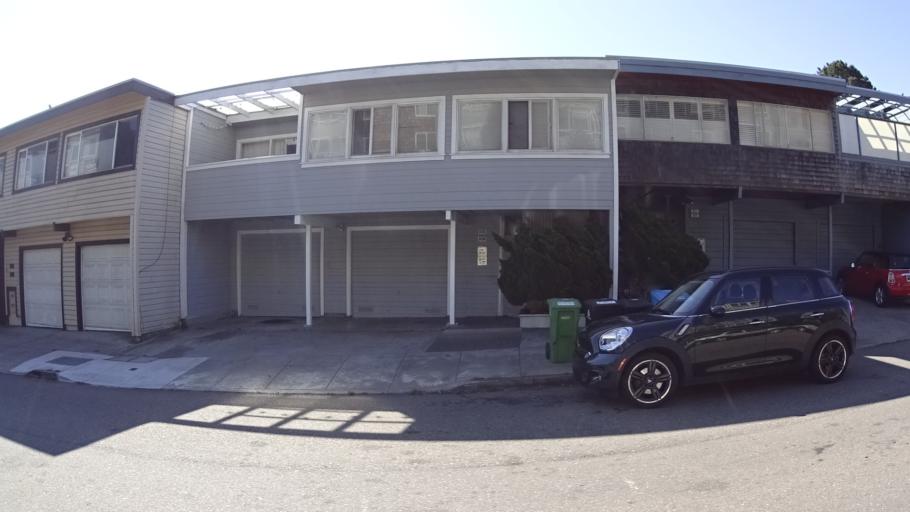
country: US
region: California
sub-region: San Francisco County
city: San Francisco
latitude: 37.7452
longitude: -122.4420
